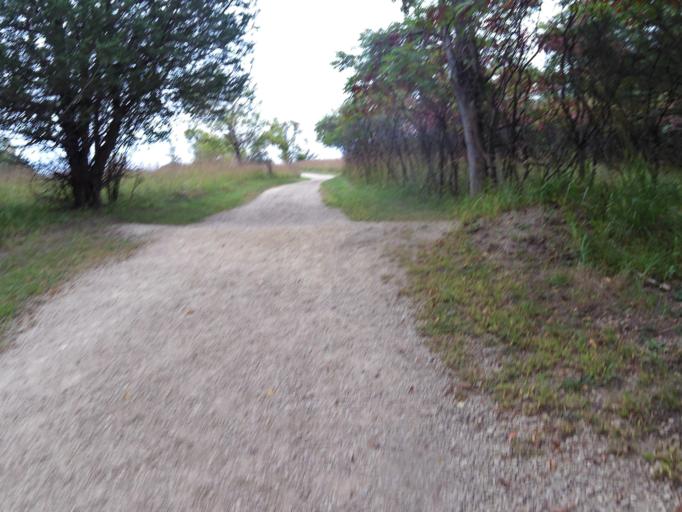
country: US
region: Minnesota
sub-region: Washington County
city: Afton
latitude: 44.8641
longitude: -92.7774
